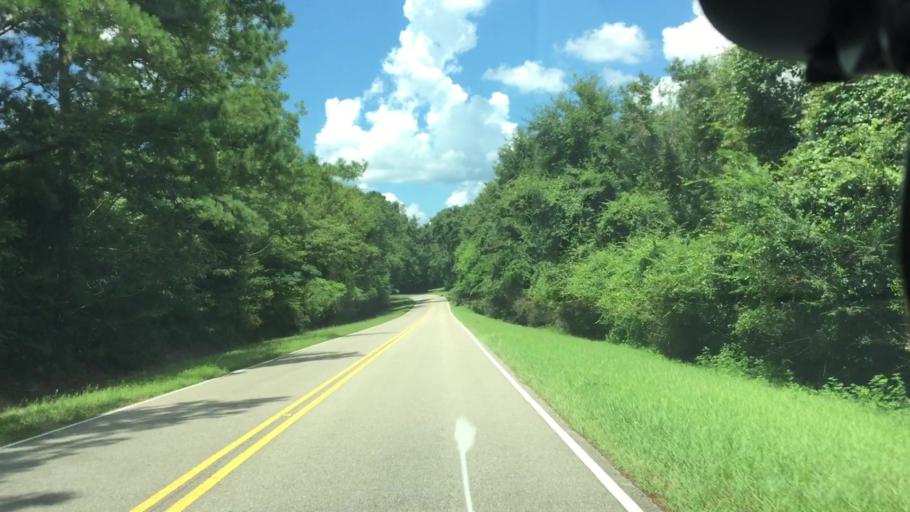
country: US
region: Alabama
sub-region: Coffee County
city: Enterprise
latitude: 31.3964
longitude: -85.8300
